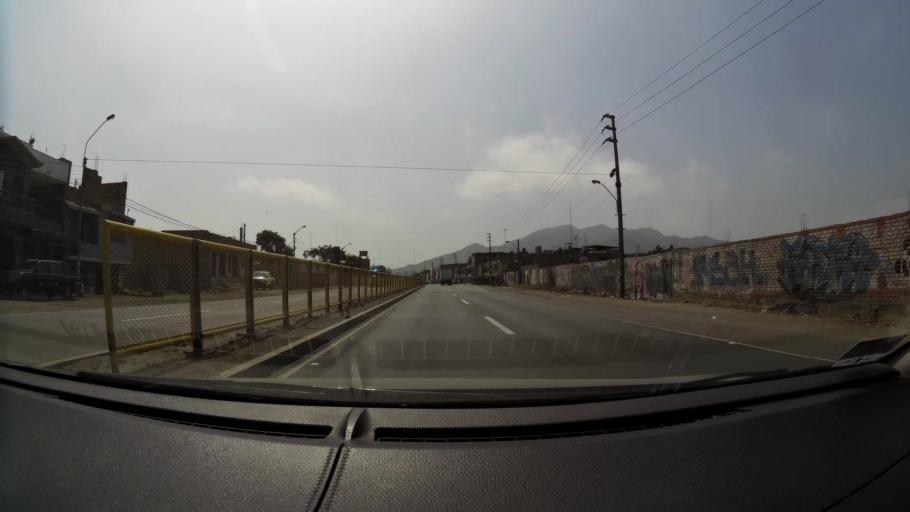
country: PE
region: Lima
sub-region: Provincia de Huaral
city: Chancay
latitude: -11.4911
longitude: -77.3042
